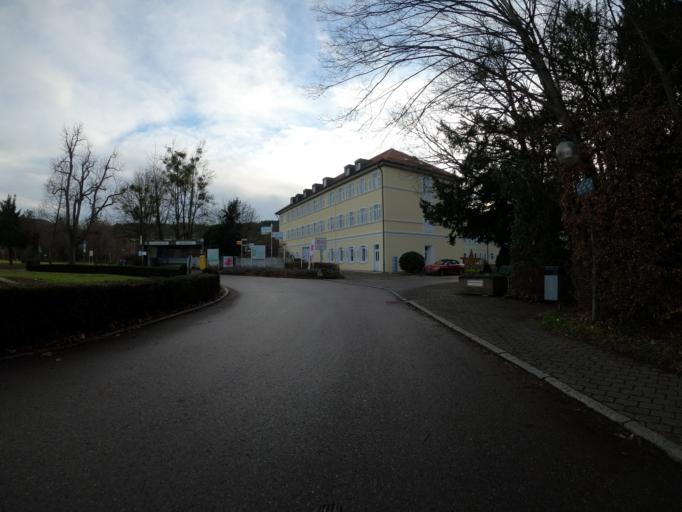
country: DE
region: Baden-Wuerttemberg
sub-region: Regierungsbezirk Stuttgart
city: Boll
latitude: 48.6401
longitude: 9.6002
